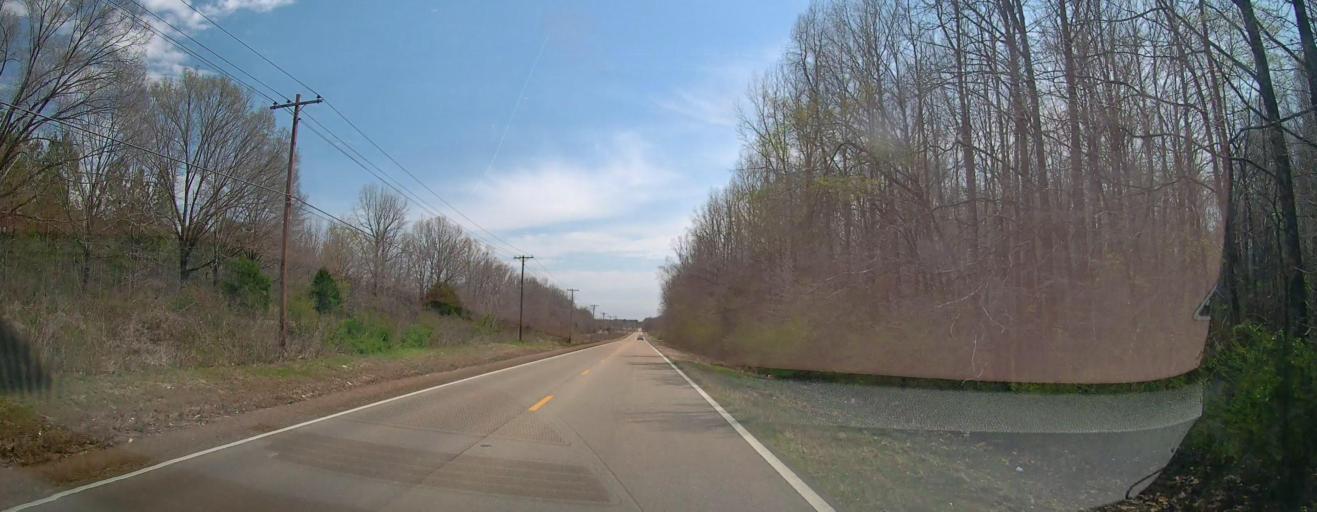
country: US
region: Mississippi
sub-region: Union County
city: New Albany
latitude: 34.5256
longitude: -89.0654
